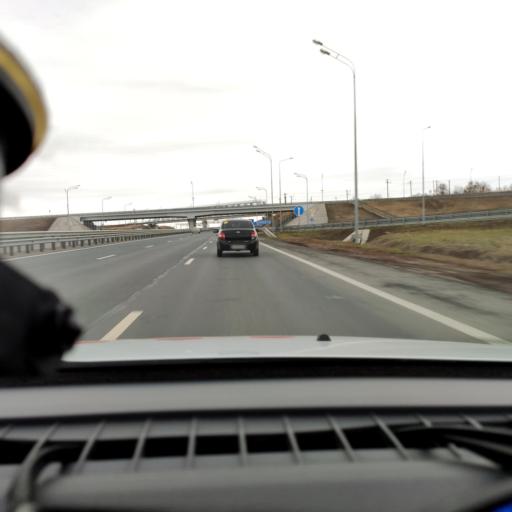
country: RU
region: Samara
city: Smyshlyayevka
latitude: 53.1489
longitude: 50.3797
